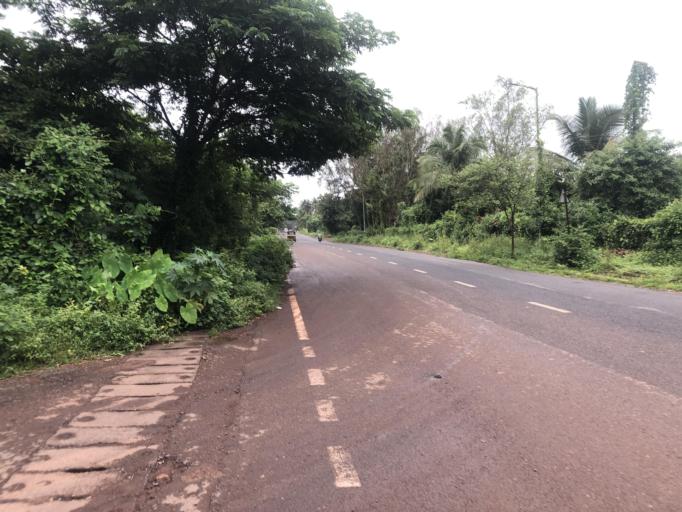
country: IN
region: Goa
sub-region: North Goa
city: Serula
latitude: 15.5375
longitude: 73.8296
